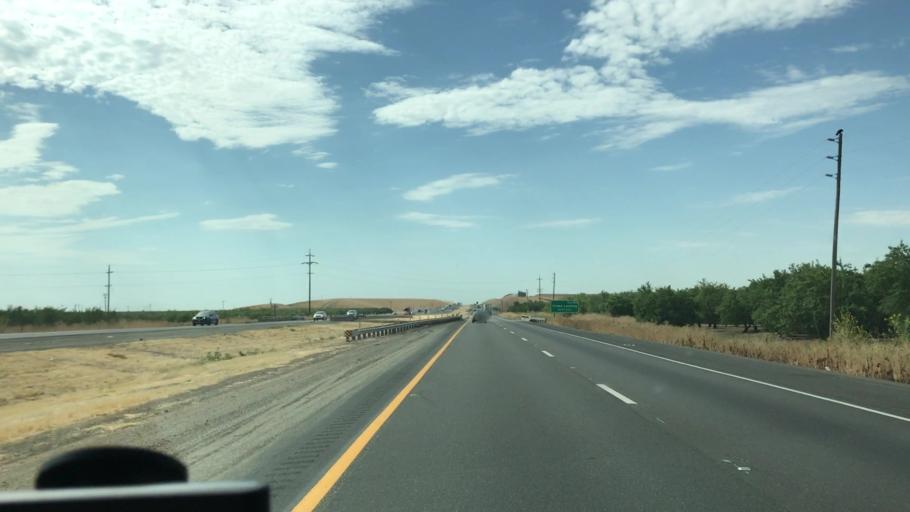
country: US
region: California
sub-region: Stanislaus County
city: Patterson
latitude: 37.4049
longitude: -121.1436
